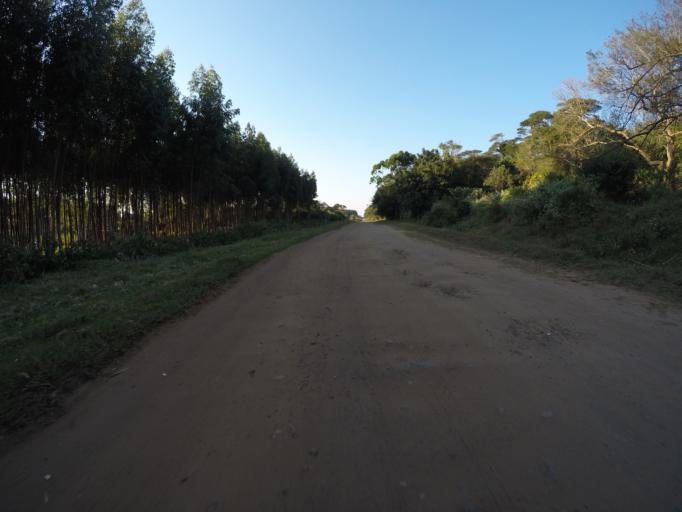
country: ZA
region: KwaZulu-Natal
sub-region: uThungulu District Municipality
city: KwaMbonambi
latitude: -28.7028
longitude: 32.1899
